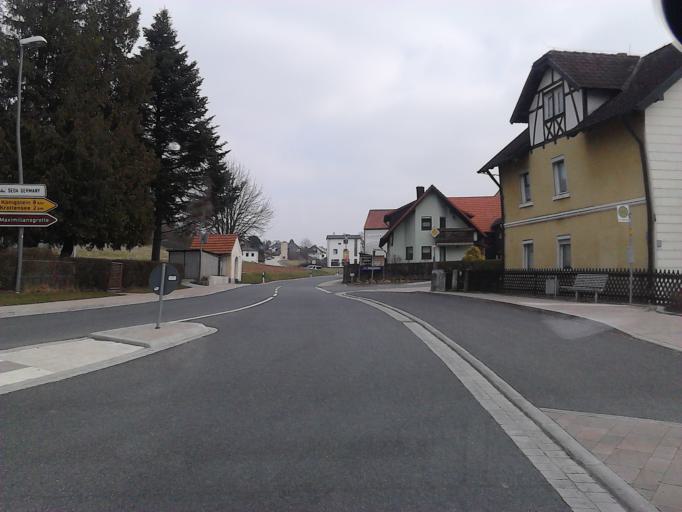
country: DE
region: Bavaria
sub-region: Regierungsbezirk Mittelfranken
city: Neuhaus an der Pegnitz
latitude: 49.6304
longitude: 11.5543
